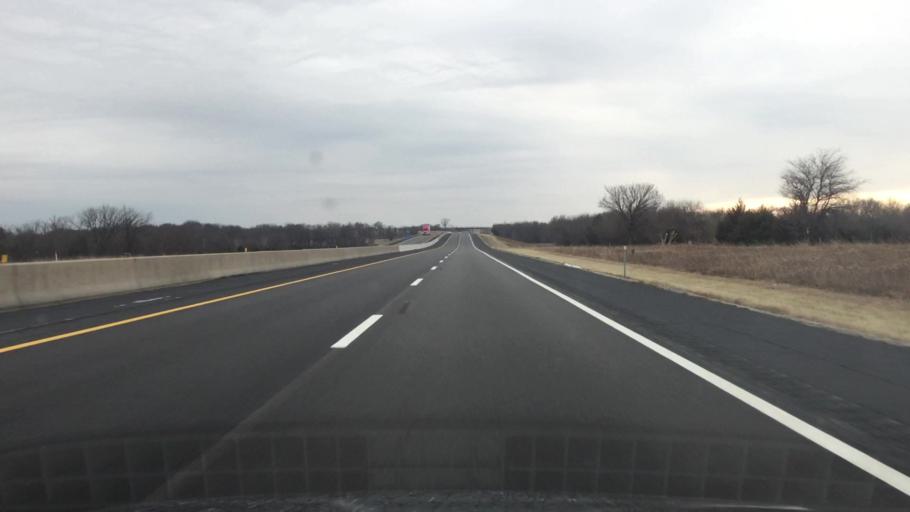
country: US
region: Kansas
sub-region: Shawnee County
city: Auburn
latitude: 38.7776
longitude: -95.9205
